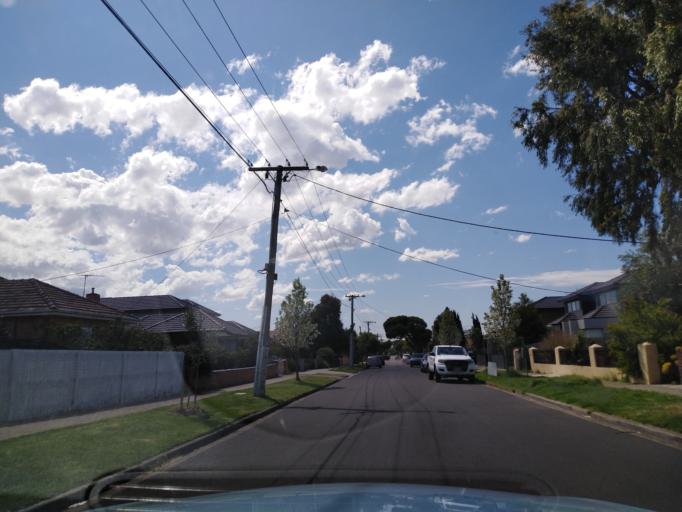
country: AU
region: Victoria
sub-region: Hobsons Bay
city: South Kingsville
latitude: -37.8327
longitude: 144.8723
